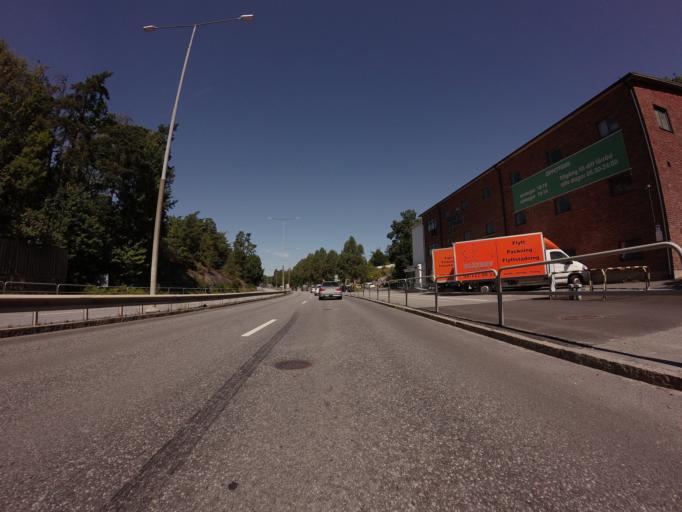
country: SE
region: Stockholm
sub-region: Lidingo
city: Lidingoe
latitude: 59.3583
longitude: 18.1361
